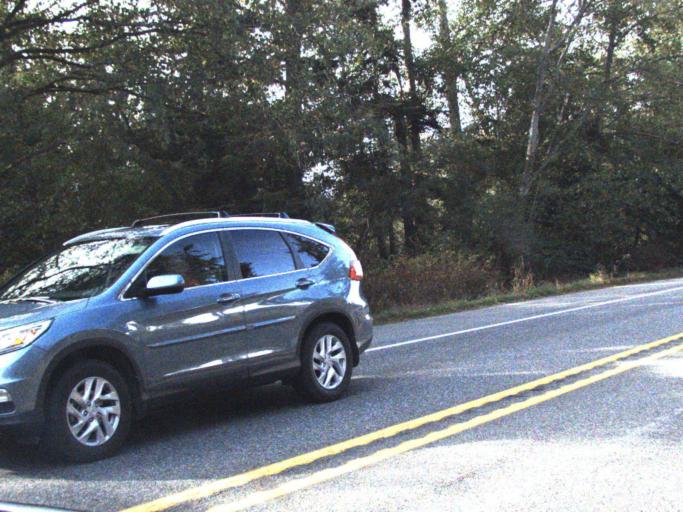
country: US
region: Washington
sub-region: Island County
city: Ault Field
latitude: 48.3641
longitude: -122.6494
